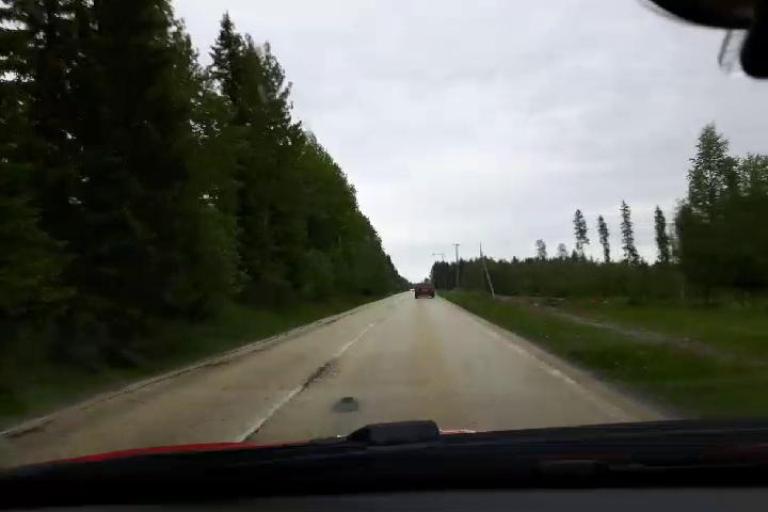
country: SE
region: Jaemtland
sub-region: Bergs Kommun
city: Hoverberg
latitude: 62.8238
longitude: 14.3926
